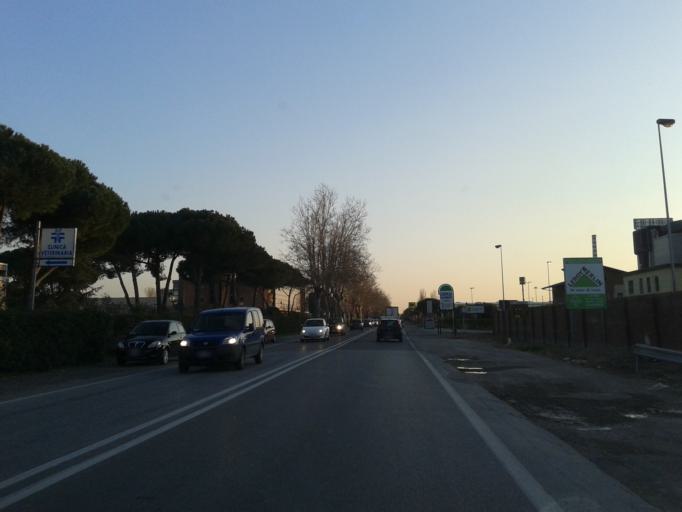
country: IT
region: Tuscany
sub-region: Provincia di Livorno
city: Livorno
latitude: 43.5910
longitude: 10.3480
